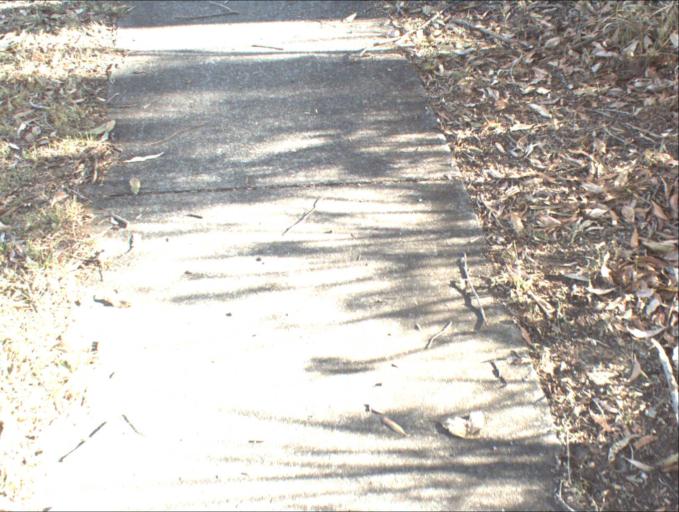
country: AU
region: Queensland
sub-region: Logan
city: Beenleigh
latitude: -27.6725
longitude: 153.2035
